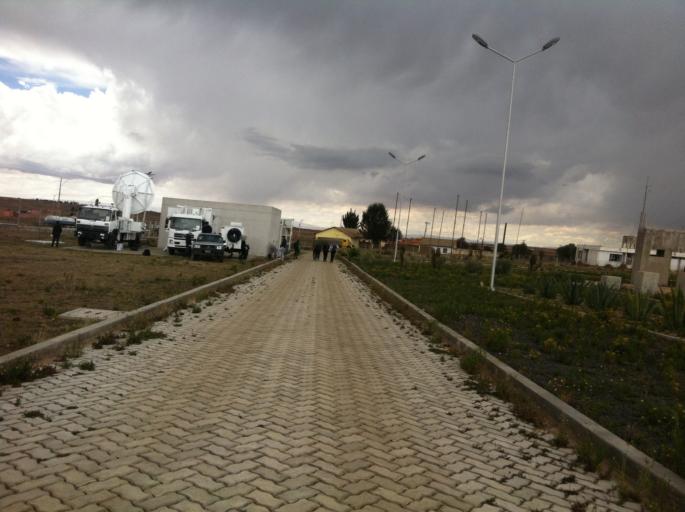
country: BO
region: La Paz
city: La Paz
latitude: -16.6231
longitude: -68.1298
